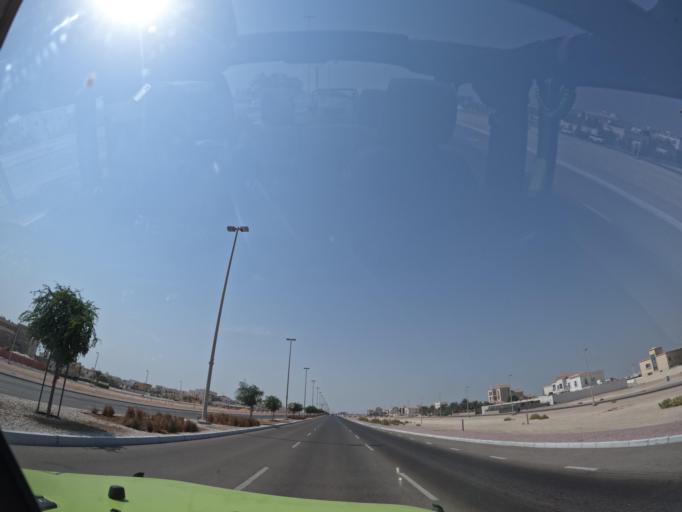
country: AE
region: Abu Dhabi
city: Abu Dhabi
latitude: 24.3524
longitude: 54.6196
